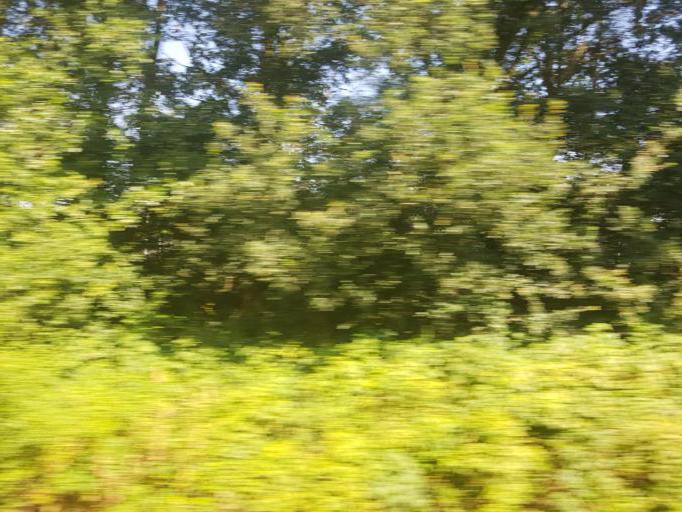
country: NL
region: Gelderland
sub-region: Gemeente Barneveld
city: Terschuur
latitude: 52.1620
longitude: 5.5131
